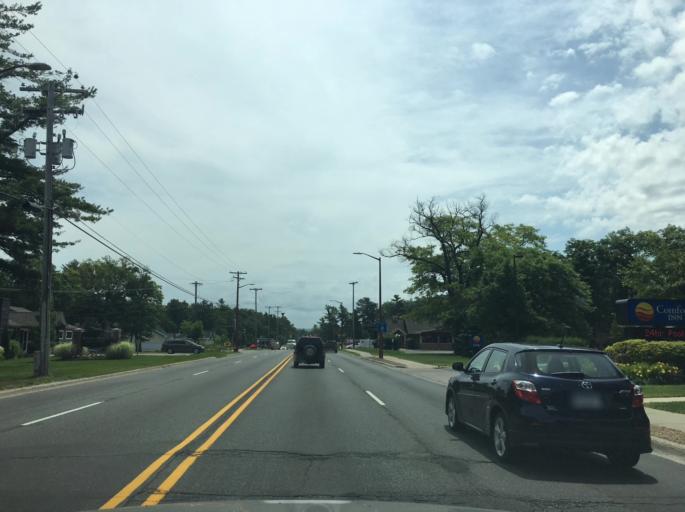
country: US
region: Michigan
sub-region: Grand Traverse County
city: Traverse City
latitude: 44.7599
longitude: -85.5812
